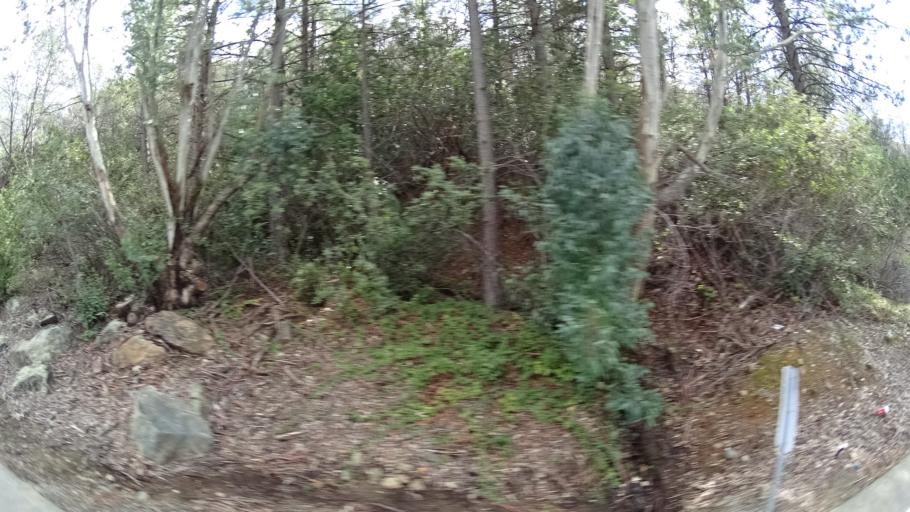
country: US
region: California
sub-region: Butte County
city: Oroville East
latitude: 39.5301
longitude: -121.4927
